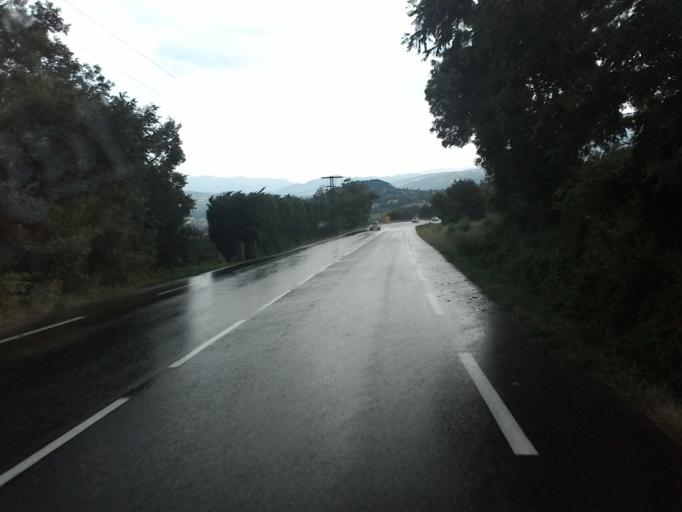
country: FR
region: Provence-Alpes-Cote d'Azur
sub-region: Departement des Hautes-Alpes
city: Gap
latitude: 44.5790
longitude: 6.0818
